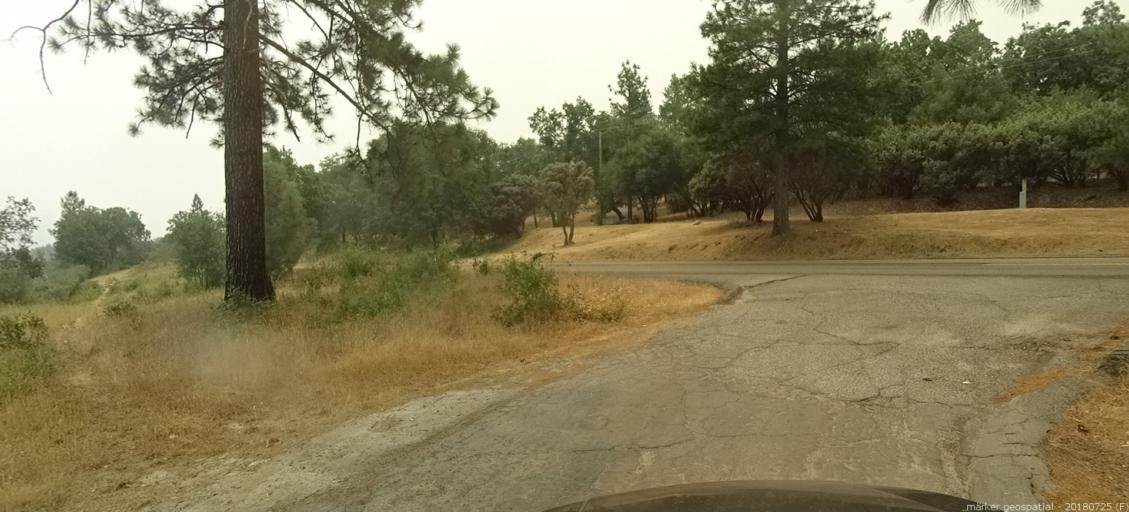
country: US
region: California
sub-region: Madera County
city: Oakhurst
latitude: 37.2627
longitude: -119.5110
